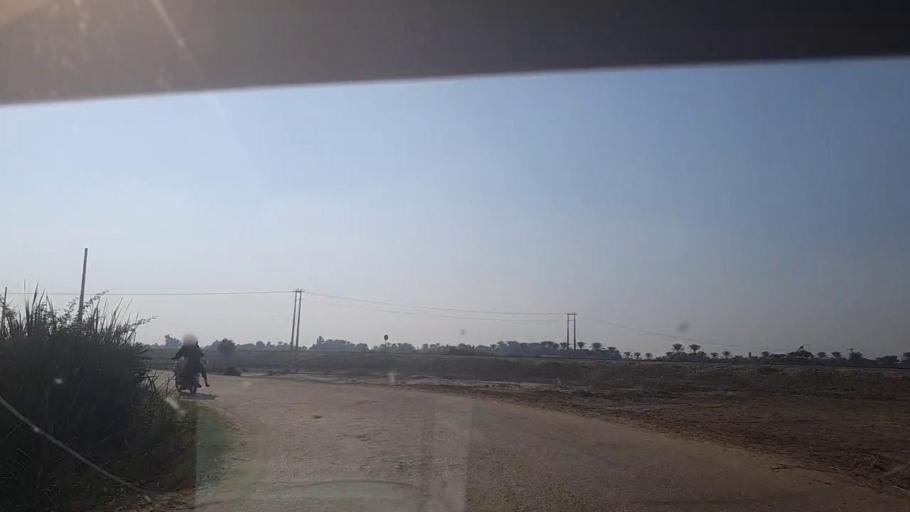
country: PK
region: Sindh
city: Gambat
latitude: 27.3627
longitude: 68.5564
